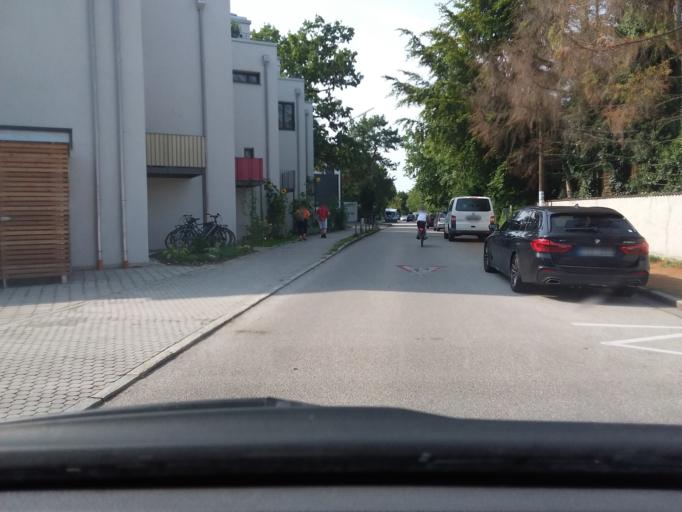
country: DE
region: Bavaria
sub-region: Upper Bavaria
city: Oberschleissheim
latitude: 48.2535
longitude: 11.5479
